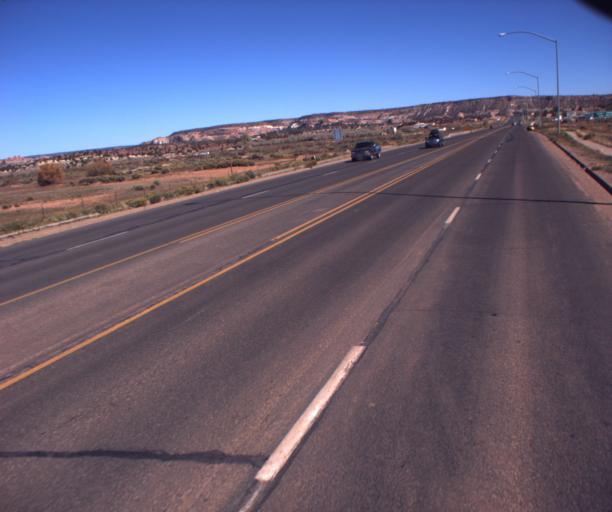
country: US
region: Arizona
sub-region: Apache County
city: Saint Michaels
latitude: 35.6588
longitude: -109.0811
